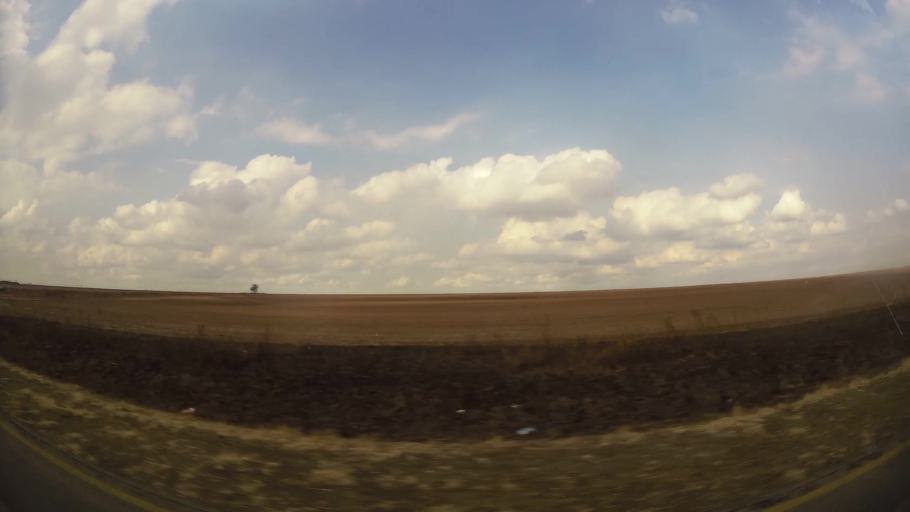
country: ZA
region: Orange Free State
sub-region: Fezile Dabi District Municipality
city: Sasolburg
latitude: -26.8338
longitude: 27.8970
